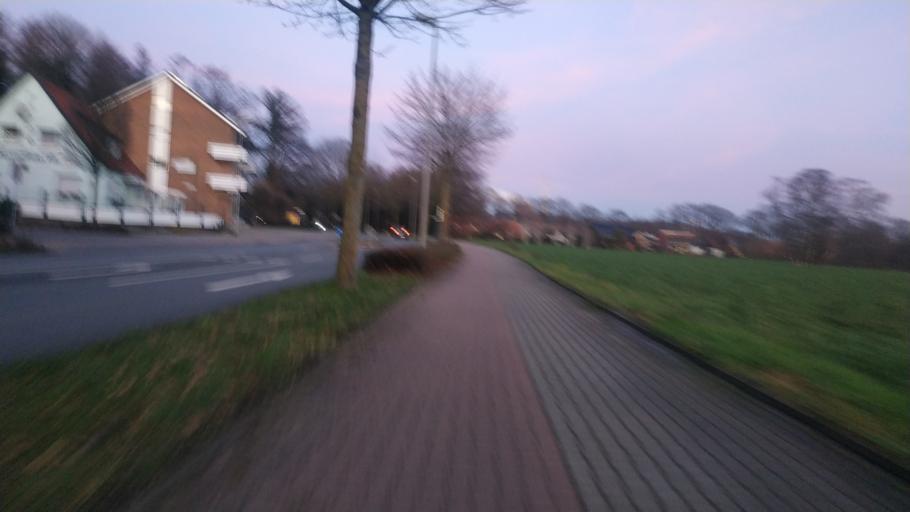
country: DE
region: North Rhine-Westphalia
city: Ibbenburen
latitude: 52.2727
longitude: 7.6925
